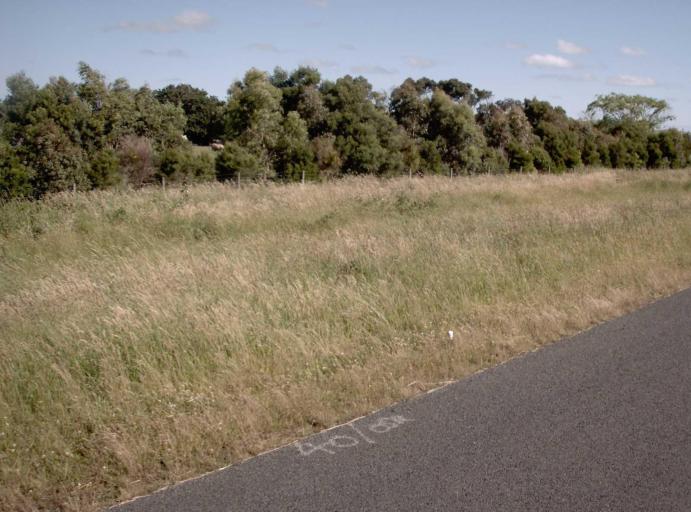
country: AU
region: Victoria
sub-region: Bass Coast
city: North Wonthaggi
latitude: -38.4734
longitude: 145.4747
